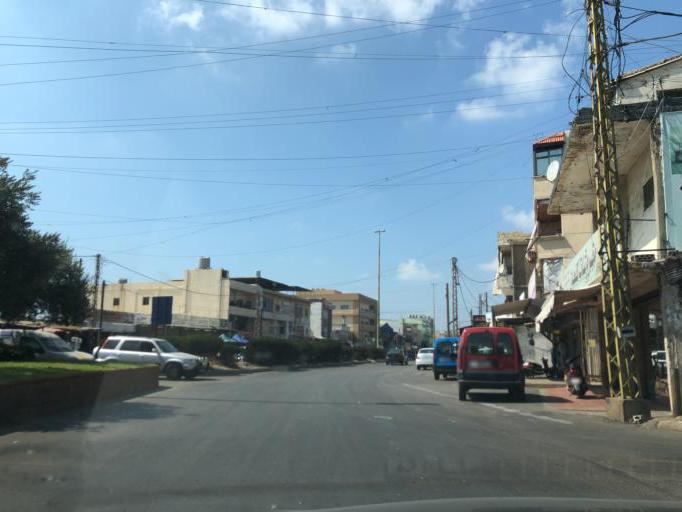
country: LB
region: Beyrouth
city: Beirut
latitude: 33.8384
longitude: 35.4848
